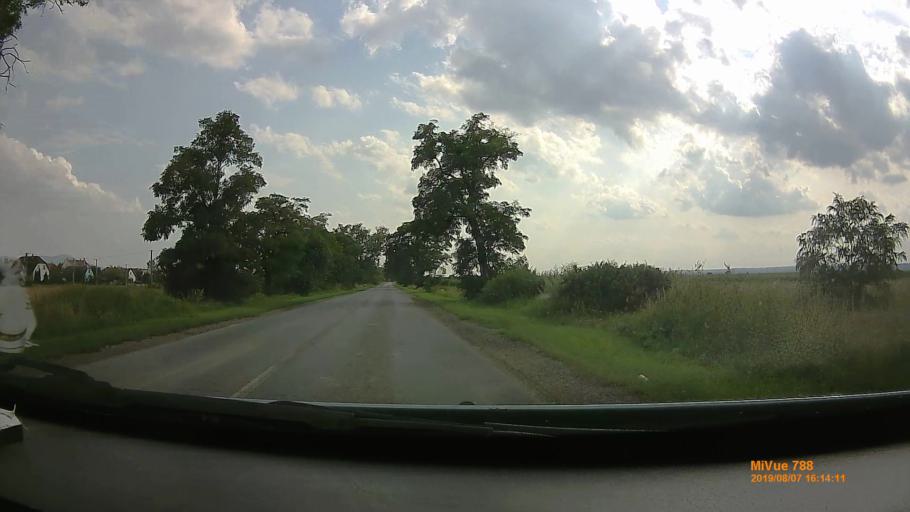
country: HU
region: Borsod-Abauj-Zemplen
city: Gonc
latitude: 48.4771
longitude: 21.2605
